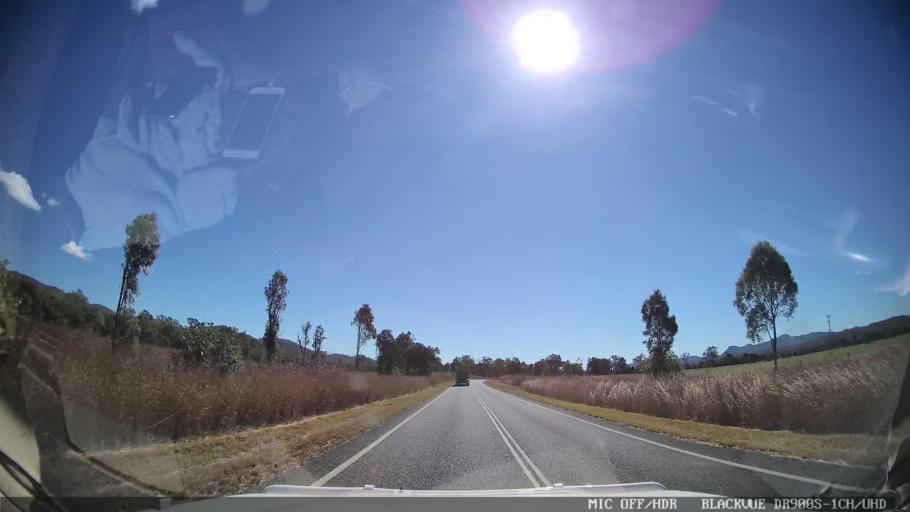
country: AU
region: Queensland
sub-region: Gladstone
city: Toolooa
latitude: -24.2787
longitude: 151.2773
